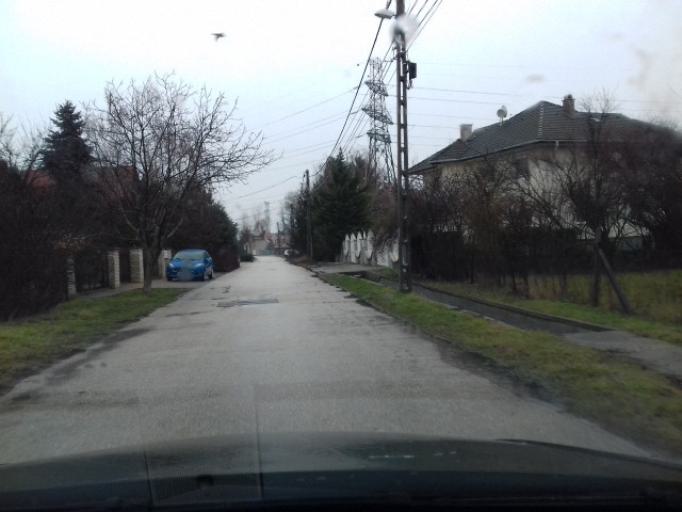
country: HU
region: Budapest
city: Budapest XXII. keruelet
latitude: 47.4334
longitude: 19.0094
